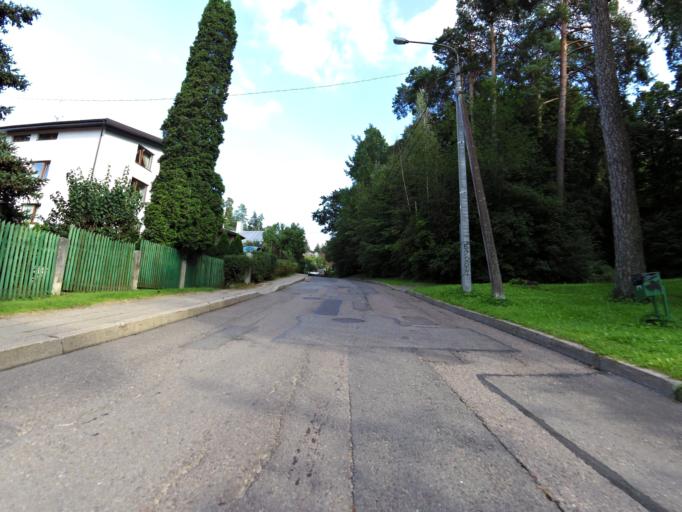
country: LT
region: Vilnius County
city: Rasos
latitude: 54.6968
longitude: 25.3160
